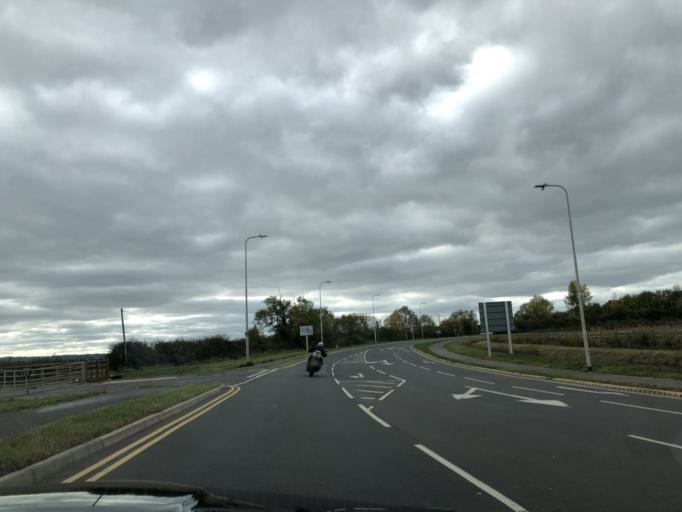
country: GB
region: England
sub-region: Warwickshire
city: Harbury
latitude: 52.1874
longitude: -1.4645
